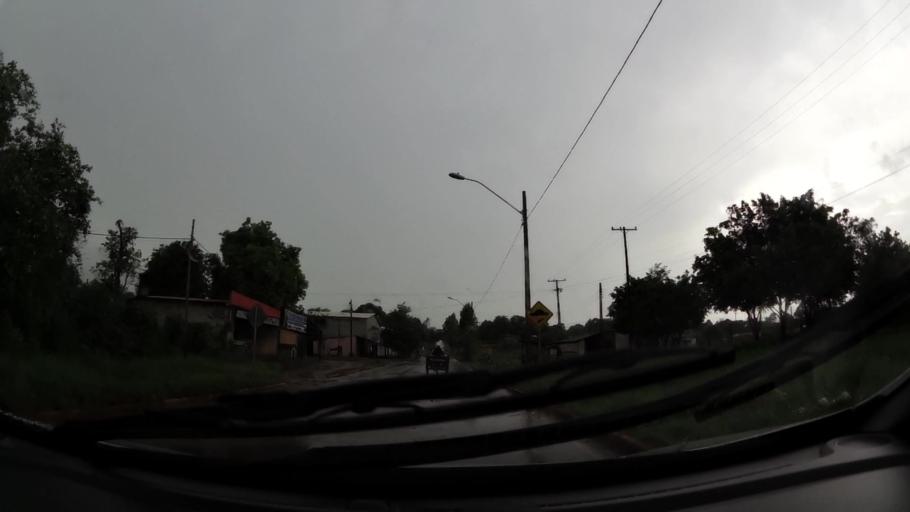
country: PY
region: Alto Parana
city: Presidente Franco
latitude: -25.5302
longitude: -54.6796
